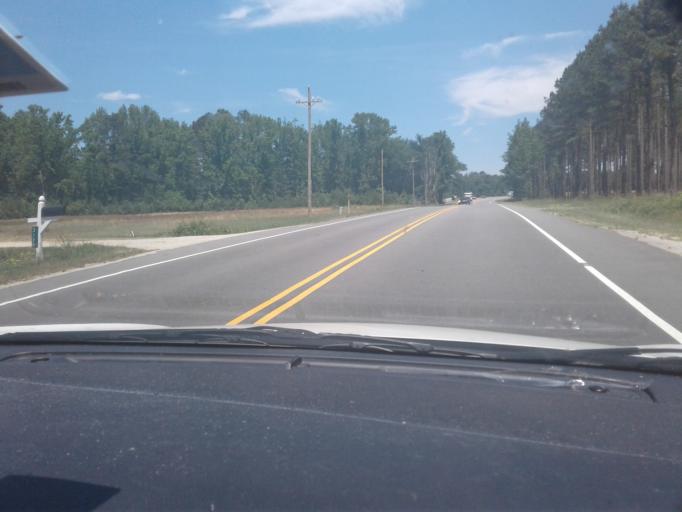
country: US
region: North Carolina
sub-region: Harnett County
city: Lillington
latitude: 35.4320
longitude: -78.8269
